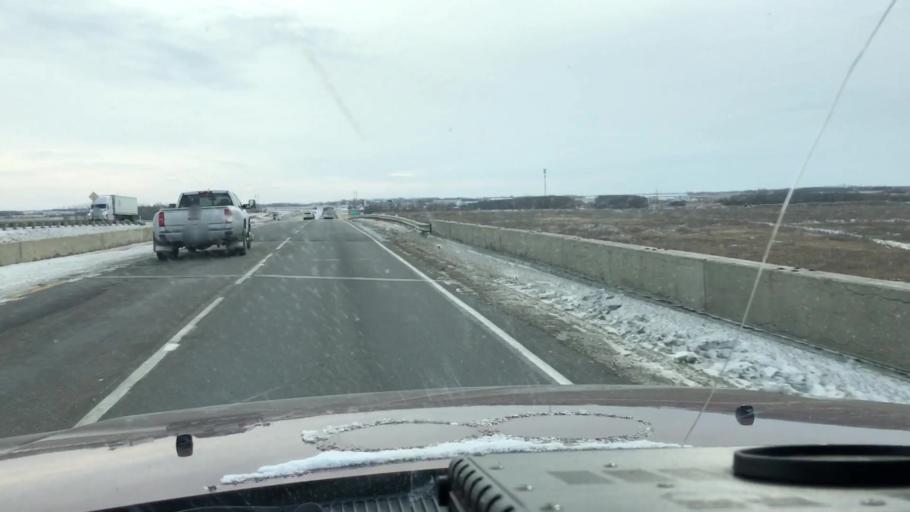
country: CA
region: Saskatchewan
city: Saskatoon
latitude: 52.0697
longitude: -106.6034
